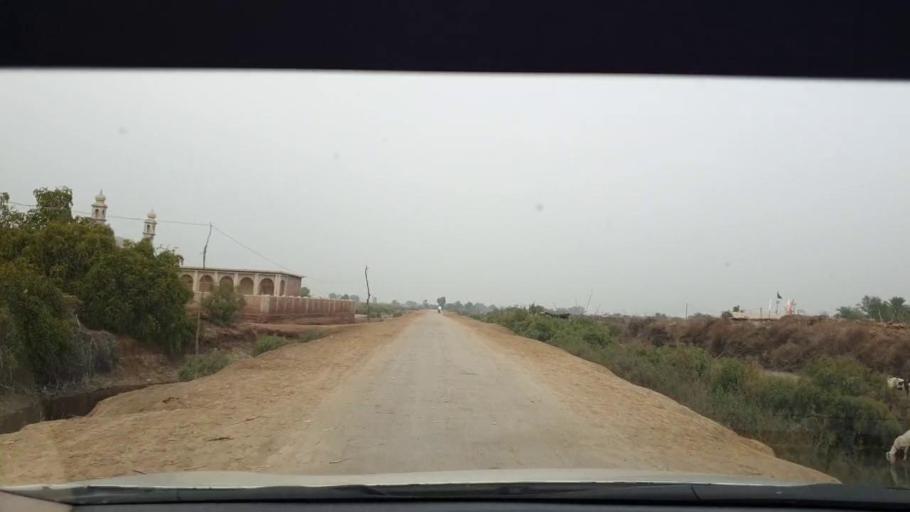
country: PK
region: Sindh
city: Berani
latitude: 25.8482
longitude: 68.8653
